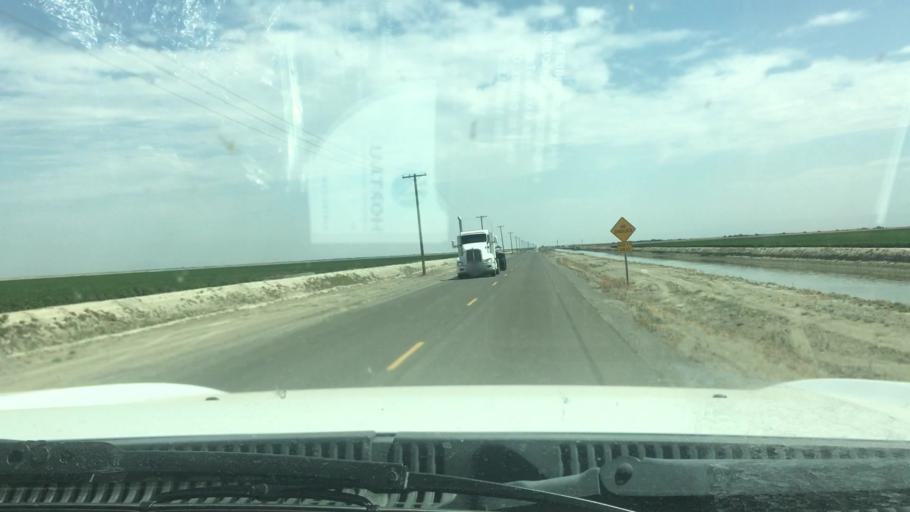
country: US
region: California
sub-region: Tulare County
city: Alpaugh
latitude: 35.8743
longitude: -119.5736
